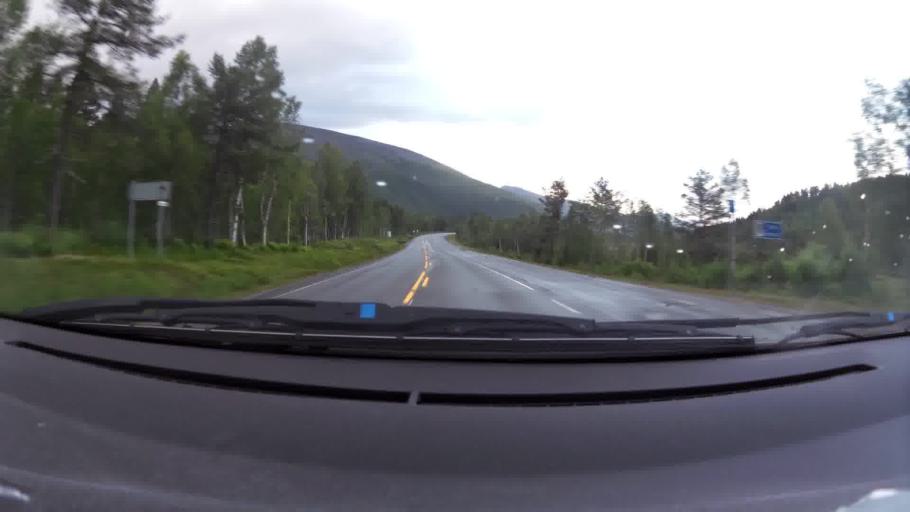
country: NO
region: More og Romsdal
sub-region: Molde
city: Molde
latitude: 62.7933
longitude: 7.3188
